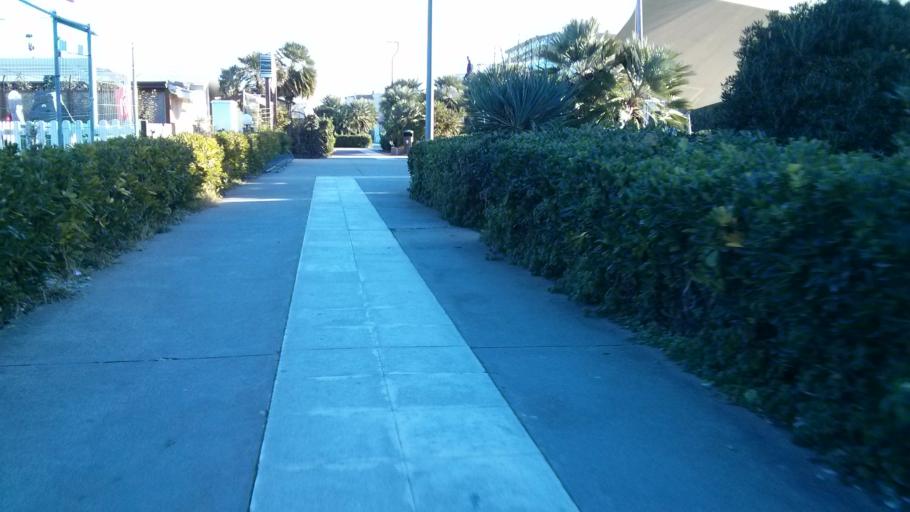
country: IT
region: The Marches
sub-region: Provincia di Pesaro e Urbino
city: Fano
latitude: 43.8490
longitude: 13.0210
